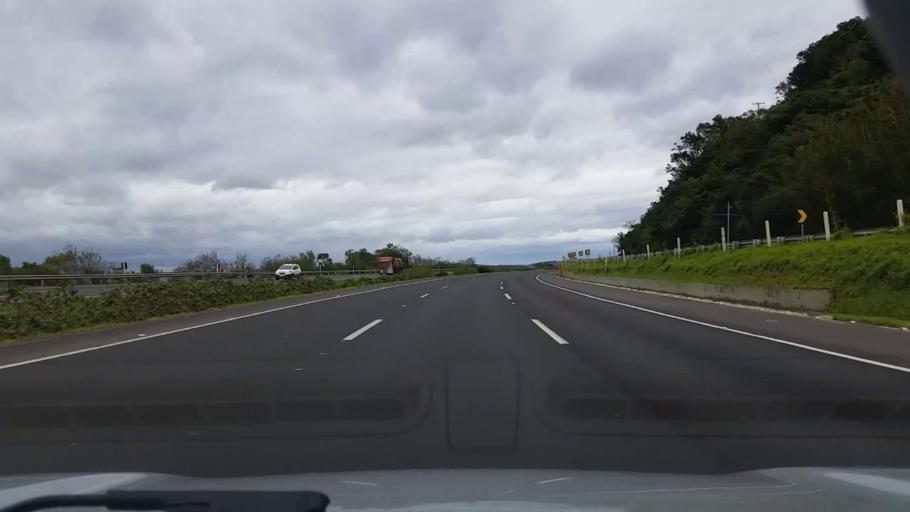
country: BR
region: Rio Grande do Sul
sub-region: Osorio
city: Osorio
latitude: -29.8973
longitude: -50.3439
